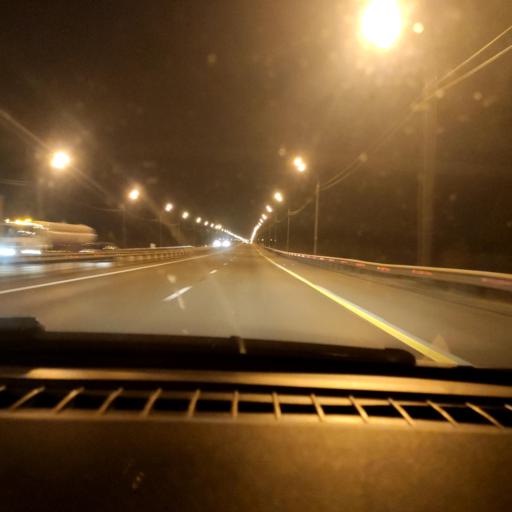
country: RU
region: Lipetsk
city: Khlevnoye
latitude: 52.1908
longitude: 39.1786
